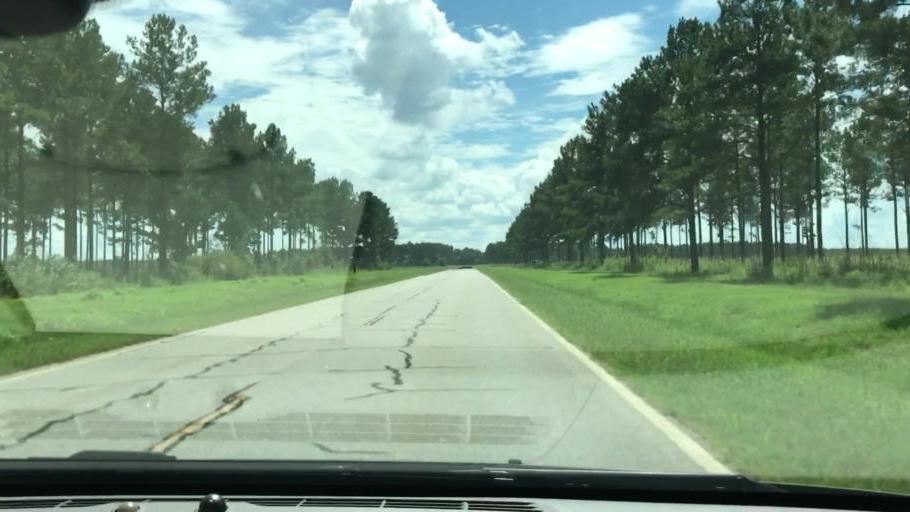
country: US
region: Georgia
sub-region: Quitman County
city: Georgetown
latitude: 32.0590
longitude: -85.0363
